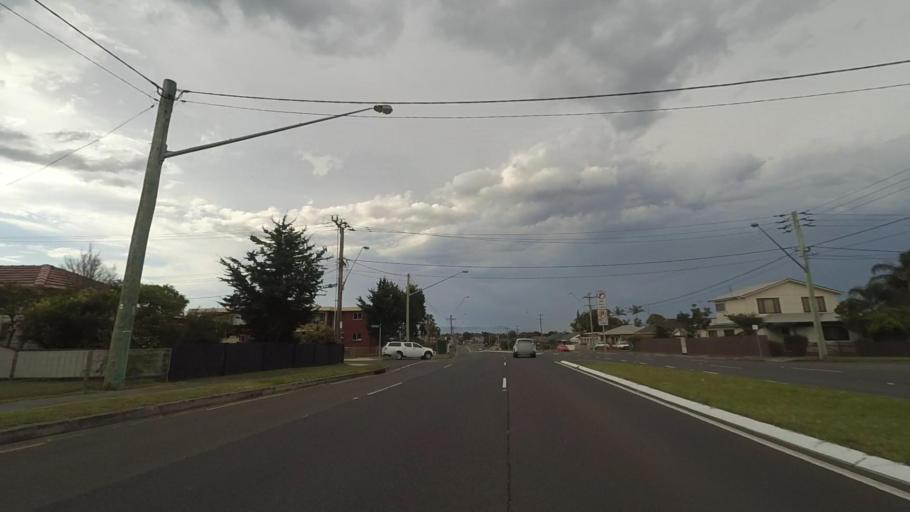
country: AU
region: New South Wales
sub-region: Shellharbour
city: Barrack Heights
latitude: -34.5622
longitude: 150.8601
